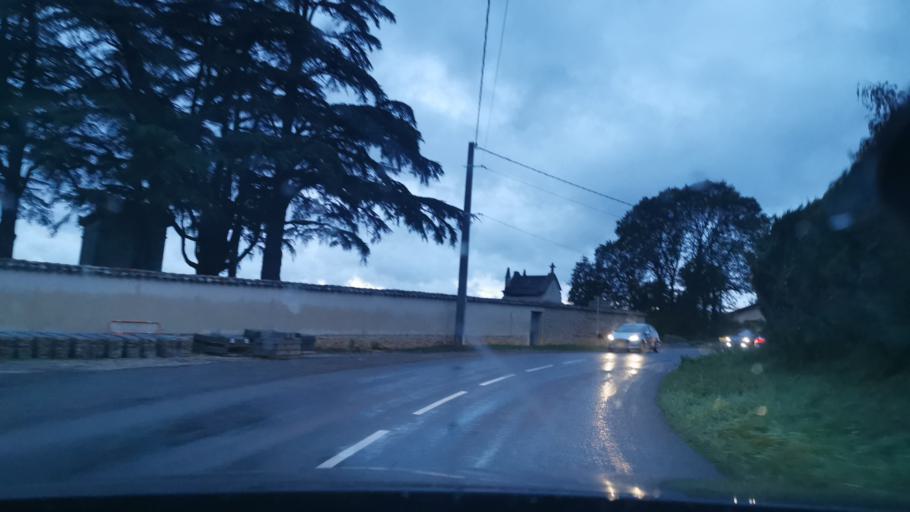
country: FR
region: Rhone-Alpes
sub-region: Departement de l'Ain
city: Crottet
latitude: 46.2678
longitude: 4.8971
